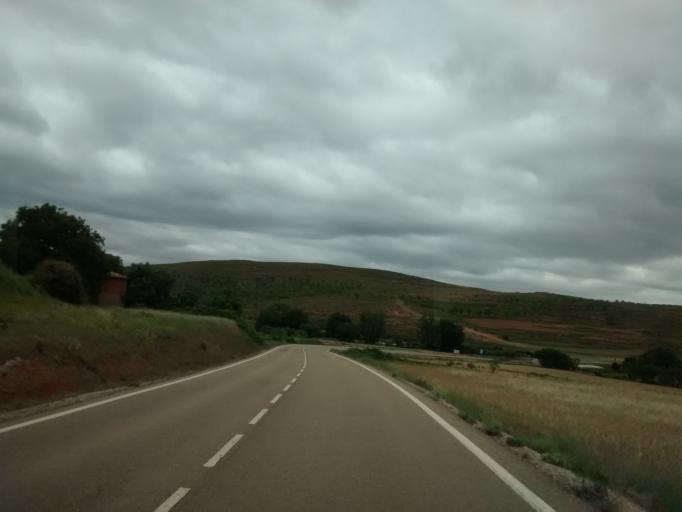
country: ES
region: Aragon
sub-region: Provincia de Zaragoza
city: Trasmoz
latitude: 41.8285
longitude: -1.7214
